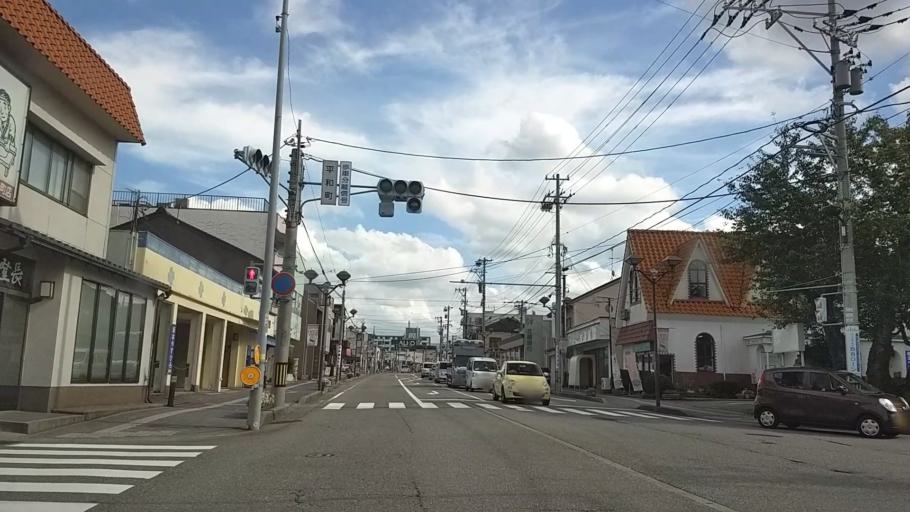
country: JP
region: Ishikawa
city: Nonoichi
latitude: 36.5427
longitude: 136.6628
